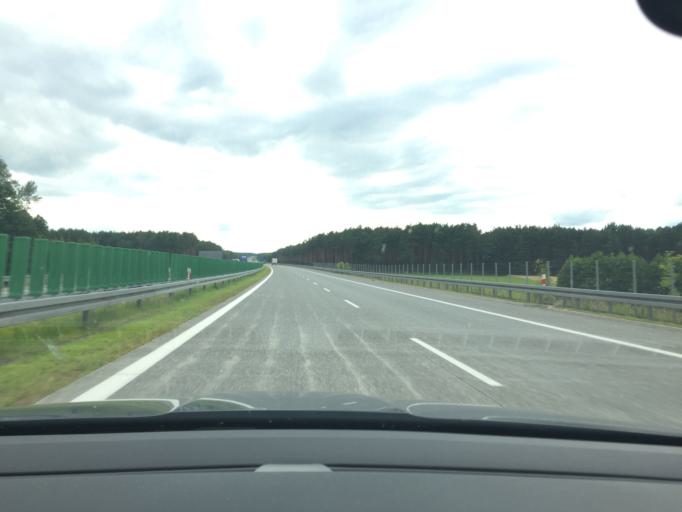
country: PL
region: Lubusz
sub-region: Powiat swiebodzinski
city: Swiebodzin
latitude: 52.3240
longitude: 15.5340
